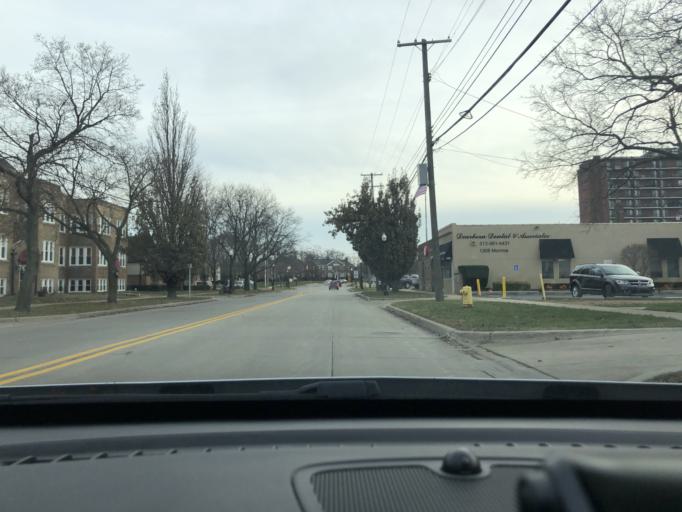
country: US
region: Michigan
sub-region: Wayne County
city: Dearborn Heights
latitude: 42.3036
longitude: -83.2430
